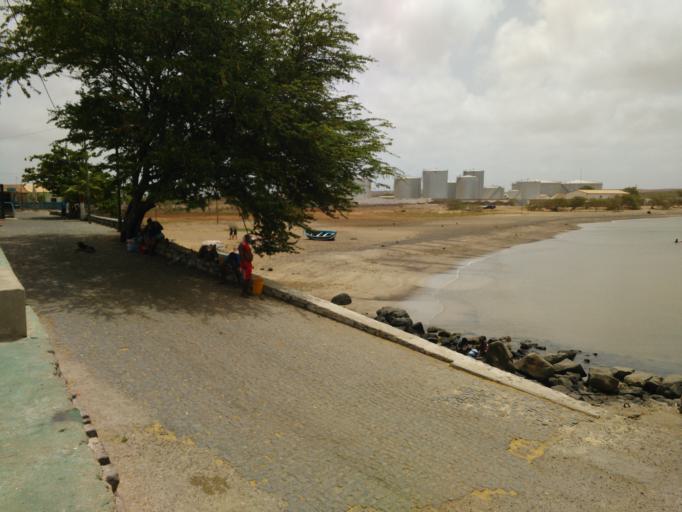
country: CV
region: Sal
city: Espargos
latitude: 16.7566
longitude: -22.9811
